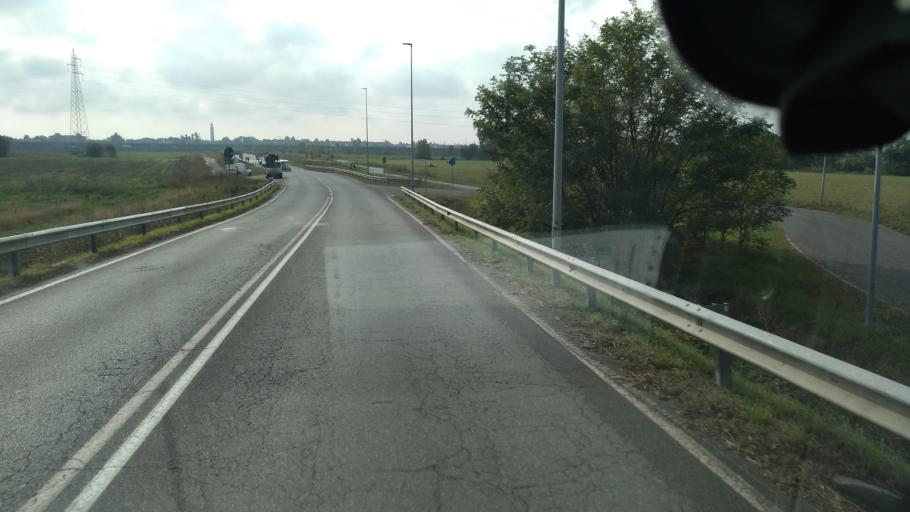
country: IT
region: Lombardy
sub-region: Provincia di Bergamo
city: Vidalengo
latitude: 45.5160
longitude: 9.6413
